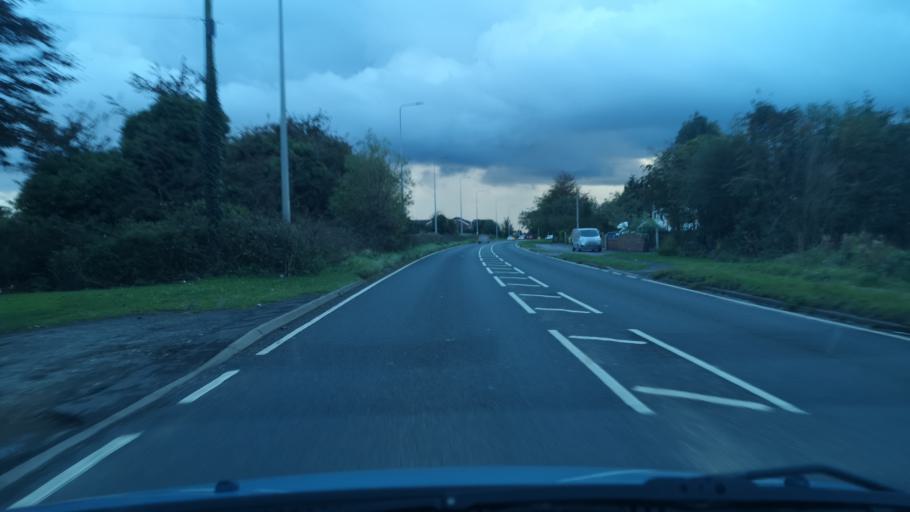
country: GB
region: England
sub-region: North Lincolnshire
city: Gunness
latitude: 53.5801
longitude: -0.7403
